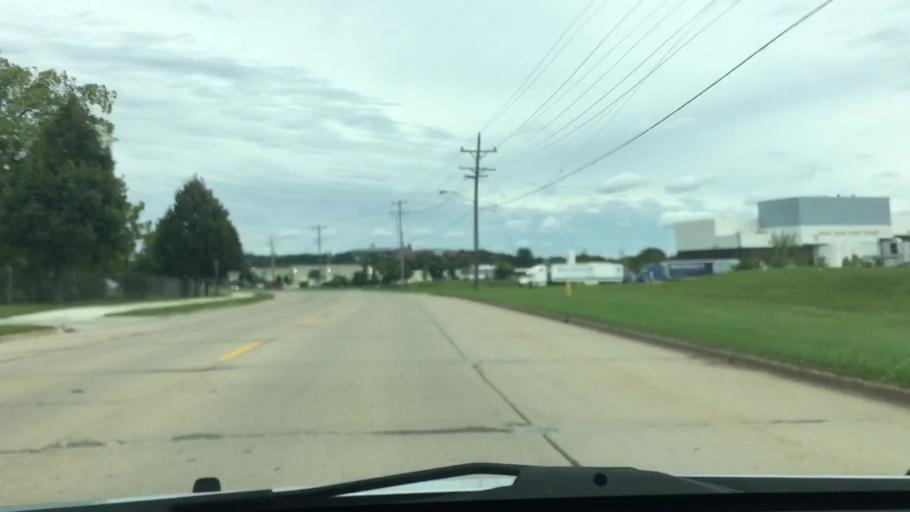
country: US
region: Wisconsin
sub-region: Waukesha County
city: Waukesha
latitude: 42.9949
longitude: -88.2495
